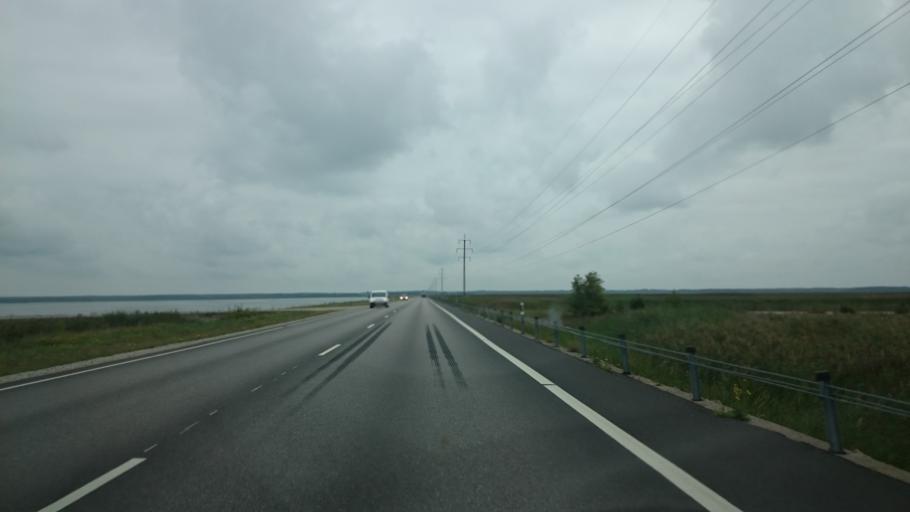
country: EE
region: Saare
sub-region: Orissaare vald
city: Orissaare
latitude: 58.5511
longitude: 23.1399
